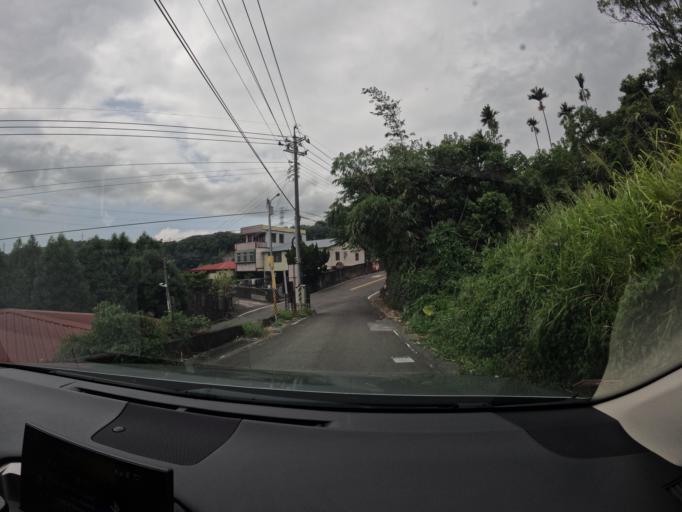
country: TW
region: Taiwan
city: Fengyuan
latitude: 24.3517
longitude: 120.8713
